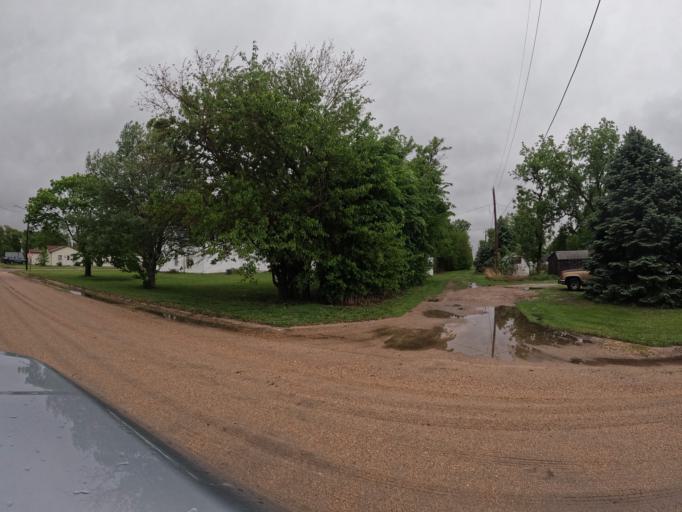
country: US
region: Nebraska
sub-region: Clay County
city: Harvard
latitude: 40.6245
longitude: -98.0979
